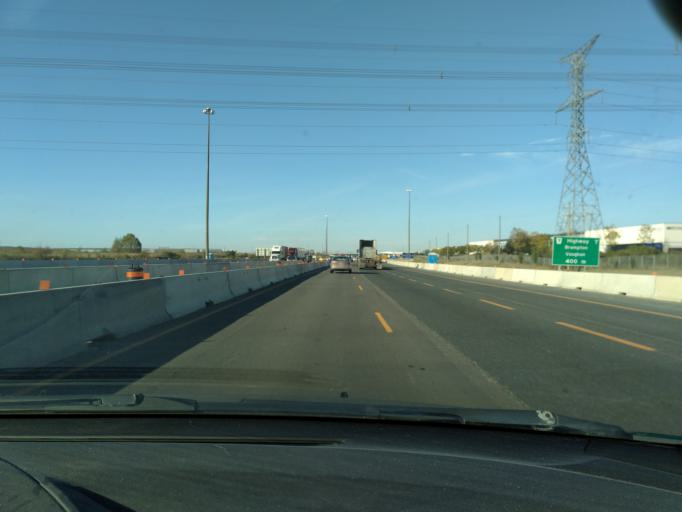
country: CA
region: Ontario
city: Etobicoke
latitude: 43.7609
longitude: -79.6321
